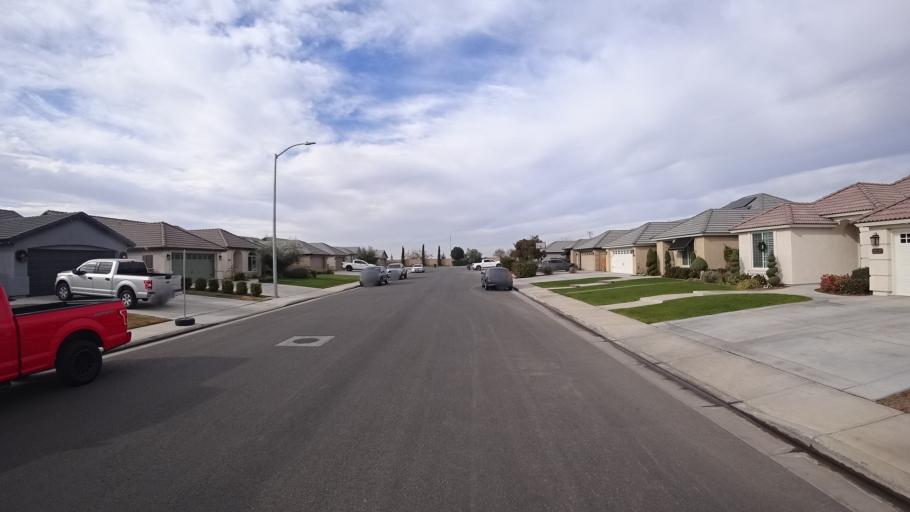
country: US
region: California
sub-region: Kern County
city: Rosedale
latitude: 35.4192
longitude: -119.1530
